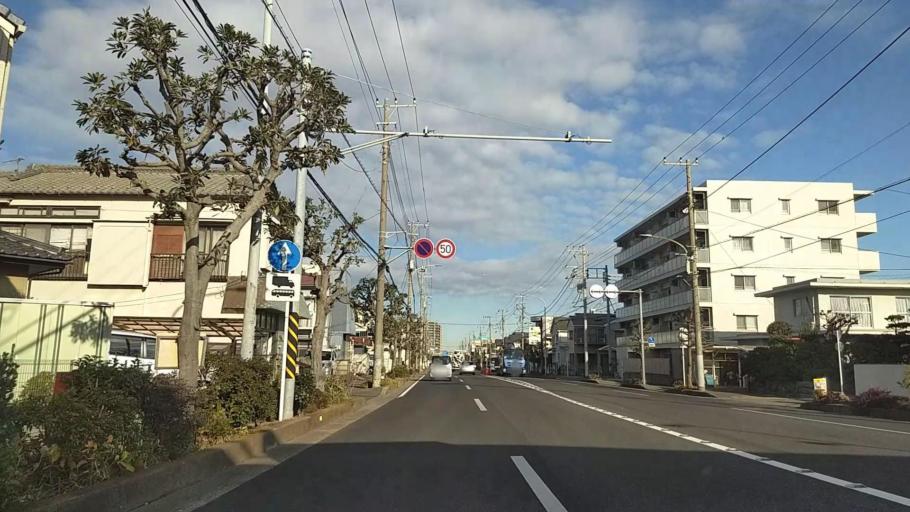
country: JP
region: Kanagawa
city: Hiratsuka
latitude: 35.3192
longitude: 139.3615
